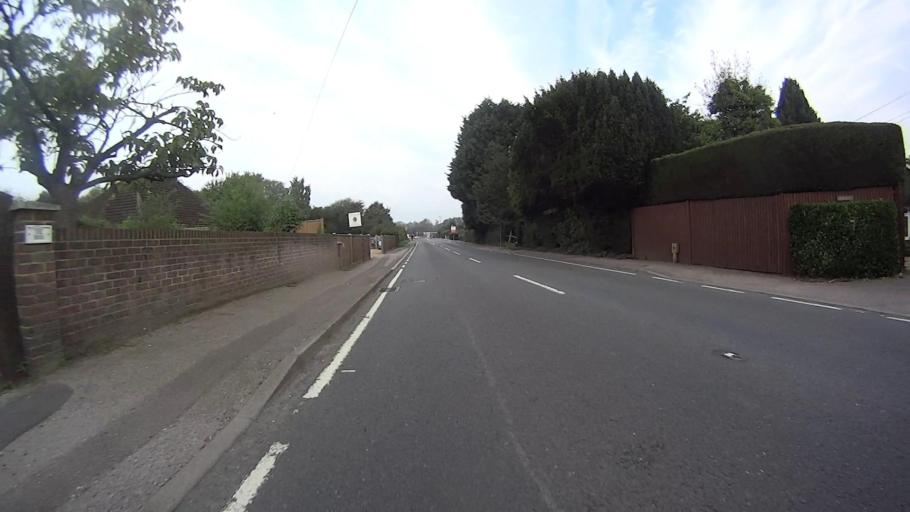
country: GB
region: England
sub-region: West Sussex
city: Copthorne
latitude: 51.1520
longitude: -0.1084
